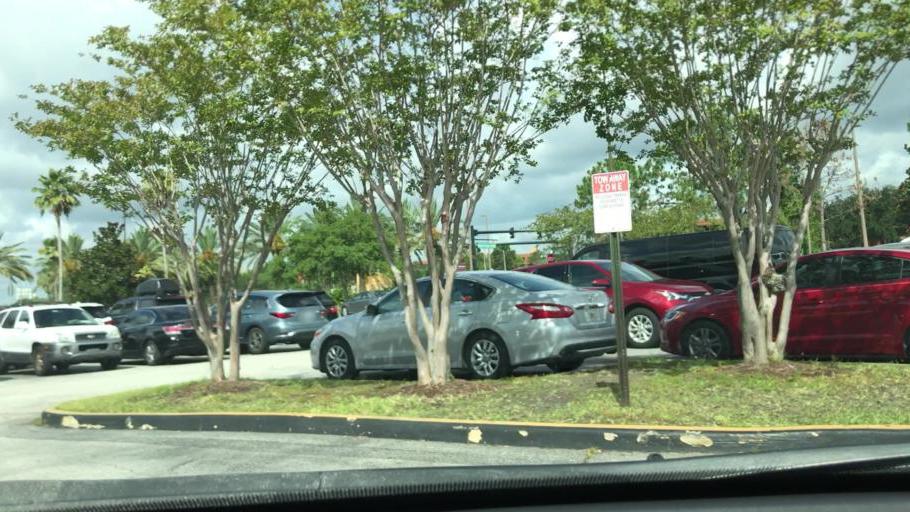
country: US
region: Florida
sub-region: Orange County
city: Williamsburg
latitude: 28.3870
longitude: -81.4943
